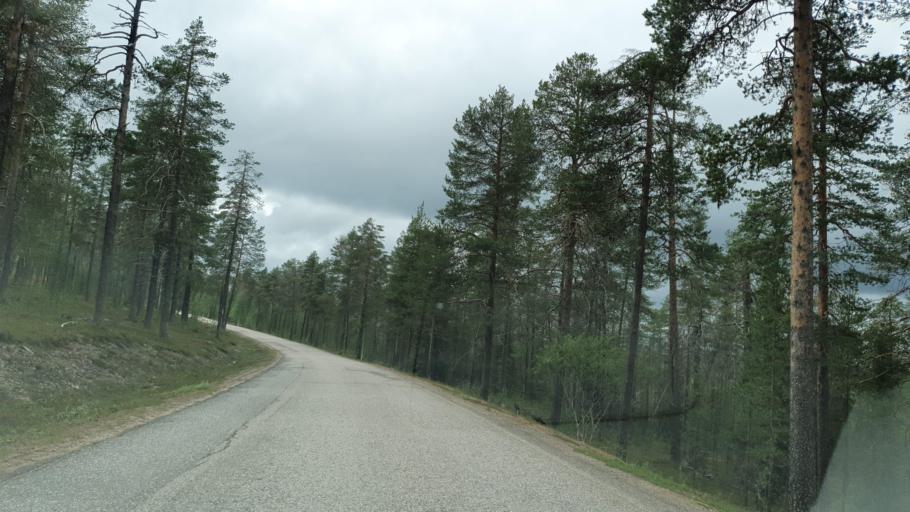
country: FI
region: Lapland
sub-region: Tunturi-Lappi
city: Kolari
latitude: 67.5273
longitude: 24.1487
